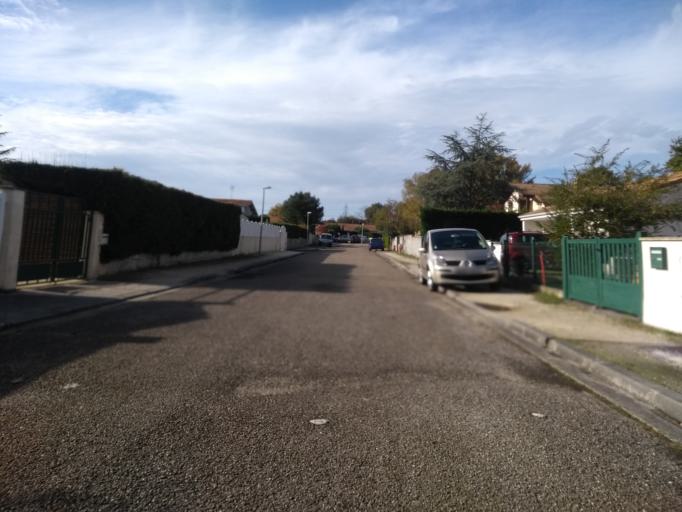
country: FR
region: Aquitaine
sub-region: Departement de la Gironde
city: Cestas
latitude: 44.7650
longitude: -0.6619
